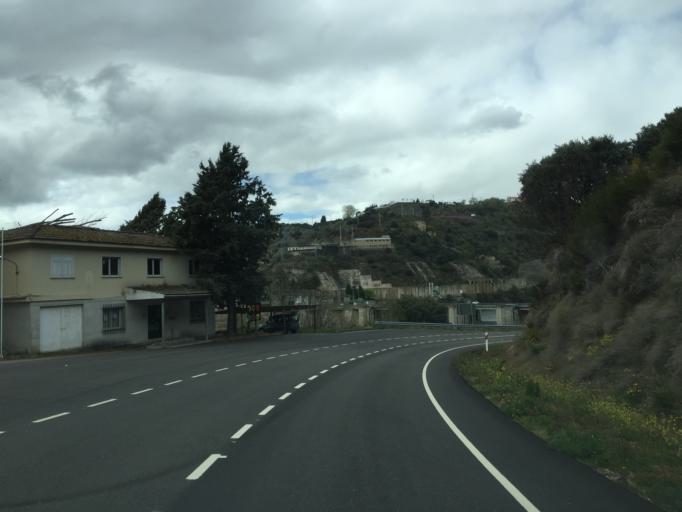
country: PT
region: Braganca
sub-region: Miranda do Douro
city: Miranda do Douro
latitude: 41.4890
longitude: -6.2608
